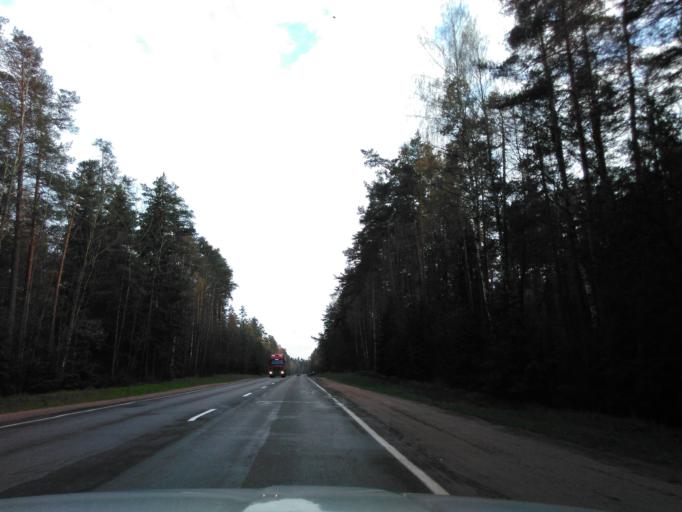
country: BY
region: Minsk
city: Plyeshchanitsy
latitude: 54.3642
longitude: 27.8837
